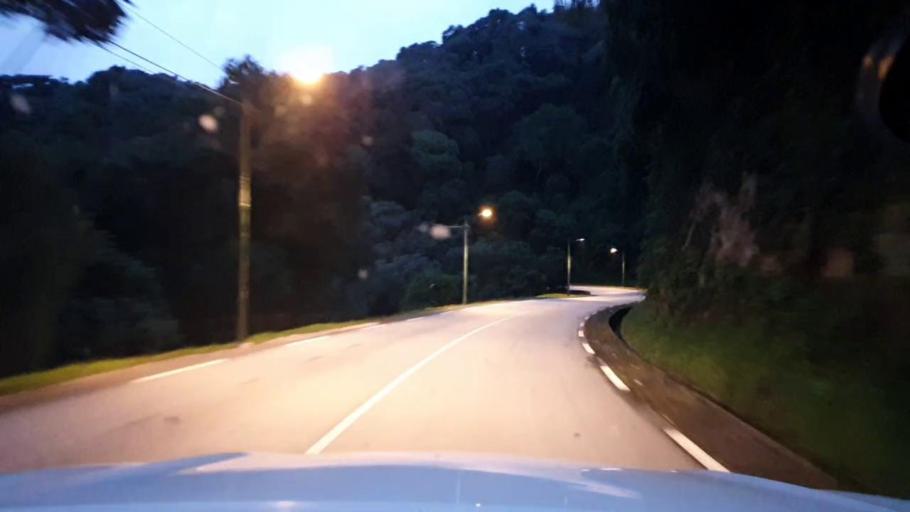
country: RW
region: Southern Province
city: Nzega
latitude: -2.5305
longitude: 29.3841
